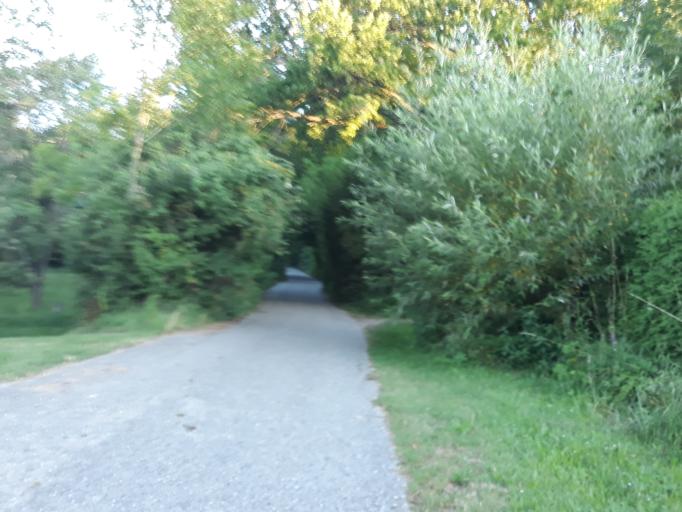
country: DE
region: Baden-Wuerttemberg
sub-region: Regierungsbezirk Stuttgart
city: Schonaich
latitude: 48.6648
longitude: 9.0438
